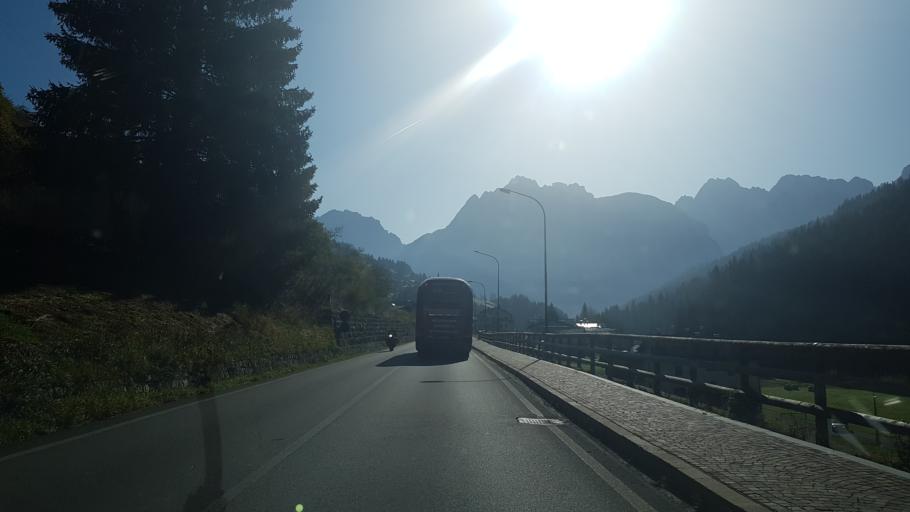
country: IT
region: Veneto
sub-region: Provincia di Belluno
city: San Nicolo Comelico
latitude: 46.5798
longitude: 12.5279
